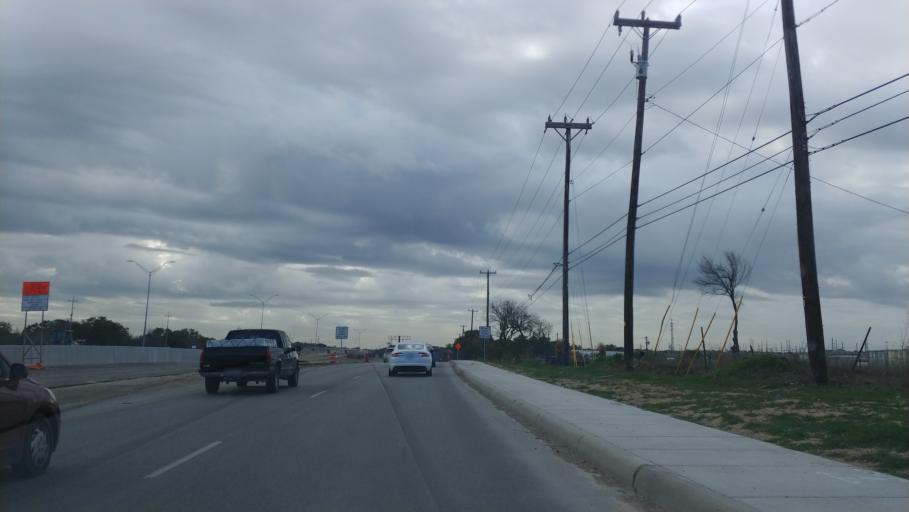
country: US
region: Texas
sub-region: Bexar County
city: Lackland Air Force Base
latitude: 29.4308
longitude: -98.7118
